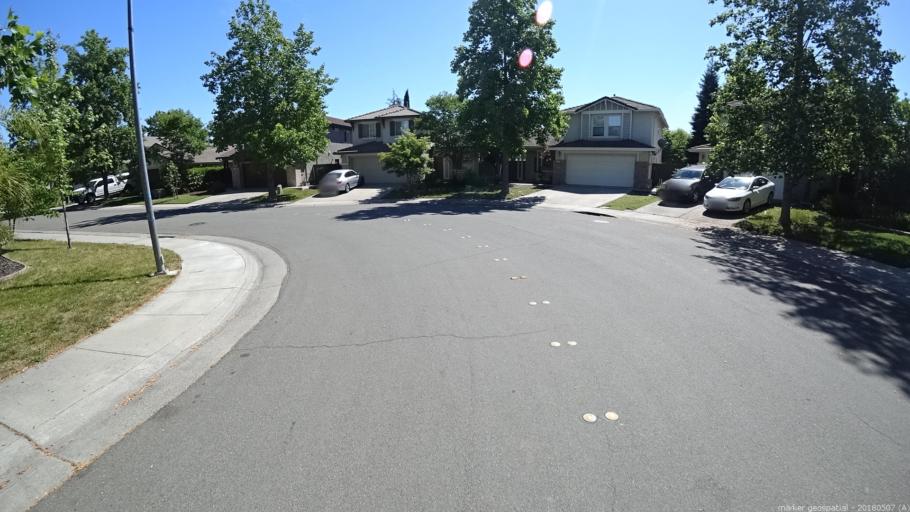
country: US
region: California
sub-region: Sacramento County
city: Rio Linda
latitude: 38.6582
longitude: -121.5003
